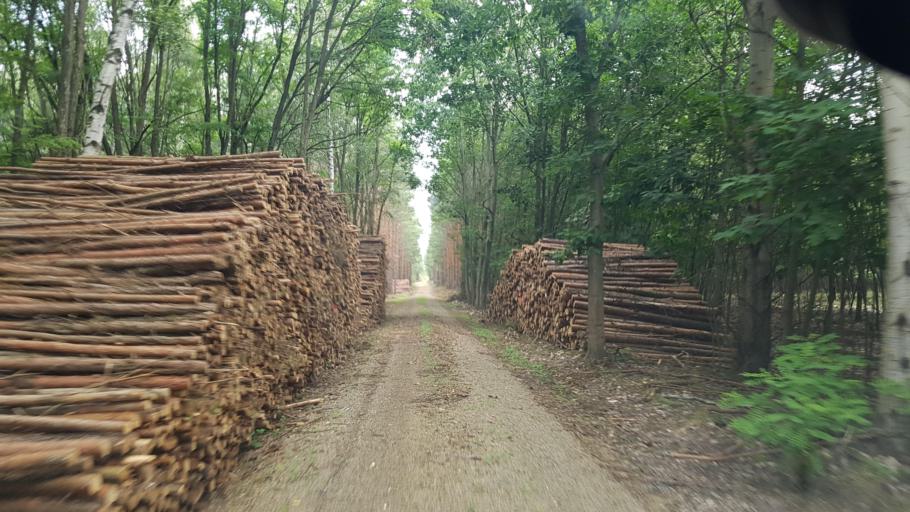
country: DE
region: Brandenburg
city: Altdobern
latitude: 51.6345
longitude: 13.9958
